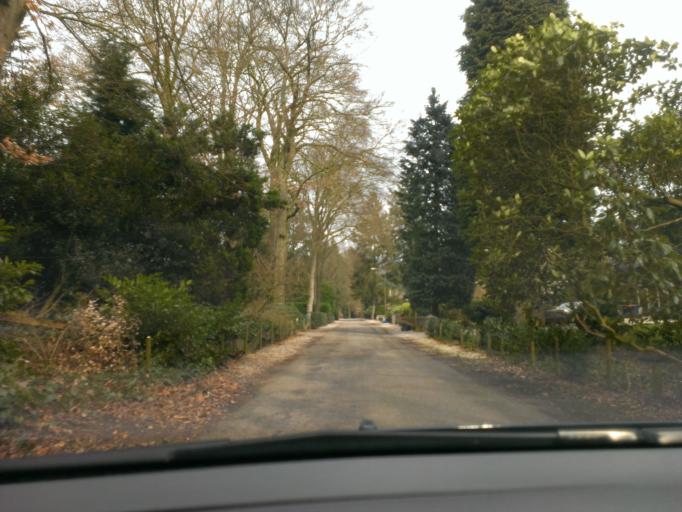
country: NL
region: Gelderland
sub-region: Gemeente Epe
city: Epe
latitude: 52.3557
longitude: 5.9914
